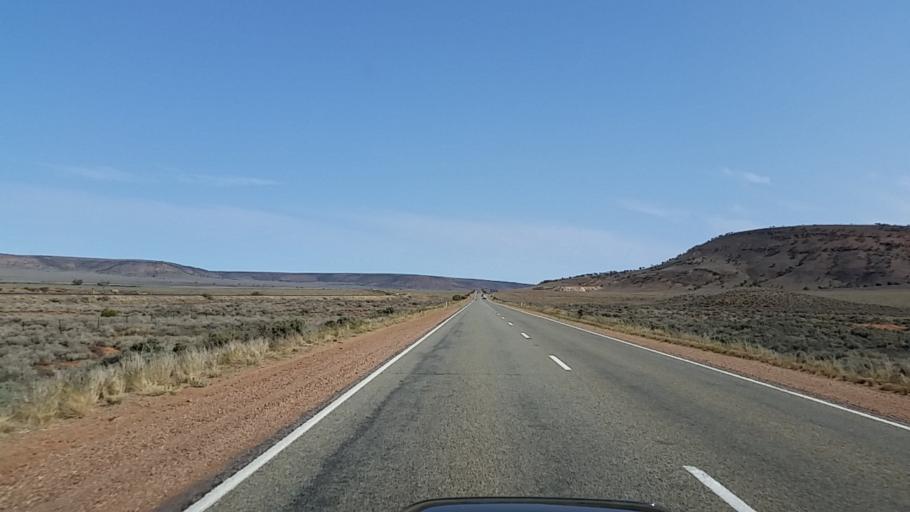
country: AU
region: South Australia
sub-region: Port Augusta
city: Port Augusta West
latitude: -32.5594
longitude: 137.6296
